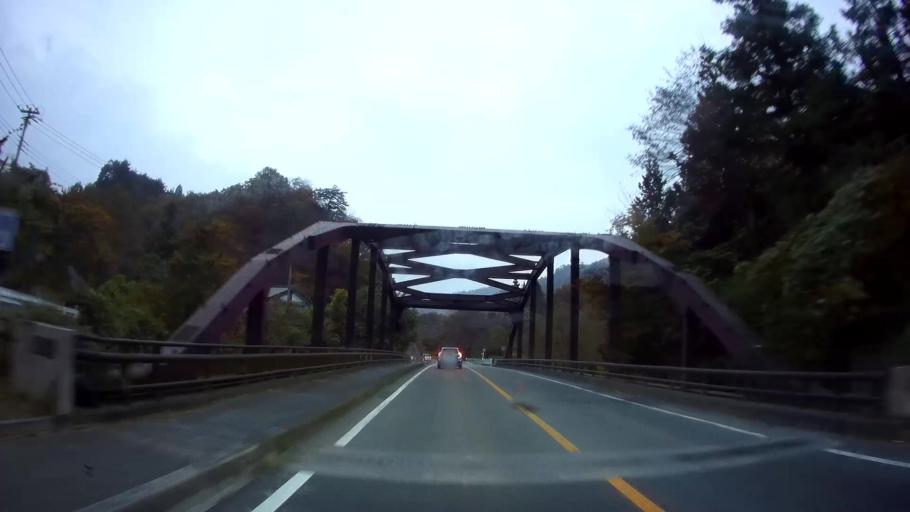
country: JP
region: Gunma
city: Nakanojomachi
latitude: 36.5295
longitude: 138.7802
